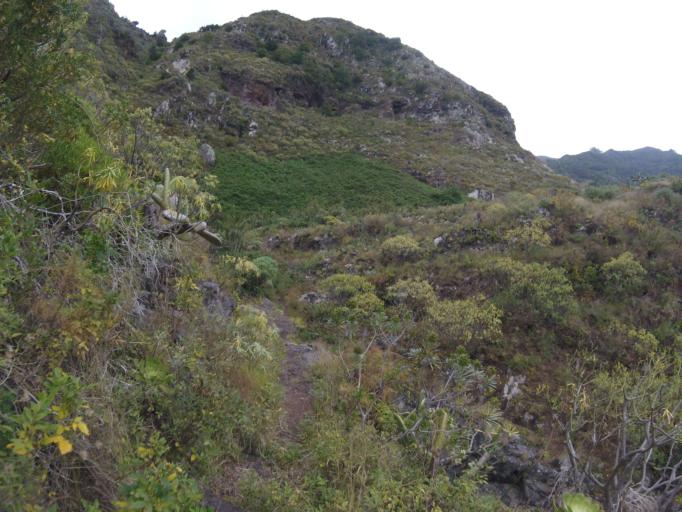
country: ES
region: Canary Islands
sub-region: Provincia de Santa Cruz de Tenerife
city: Tegueste
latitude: 28.5498
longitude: -16.2931
